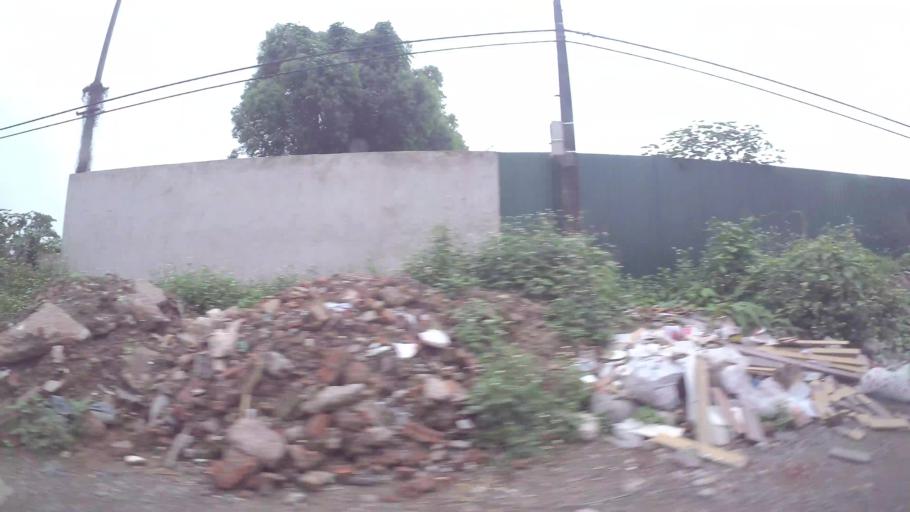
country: VN
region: Ha Noi
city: Van Dien
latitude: 20.9762
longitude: 105.8792
